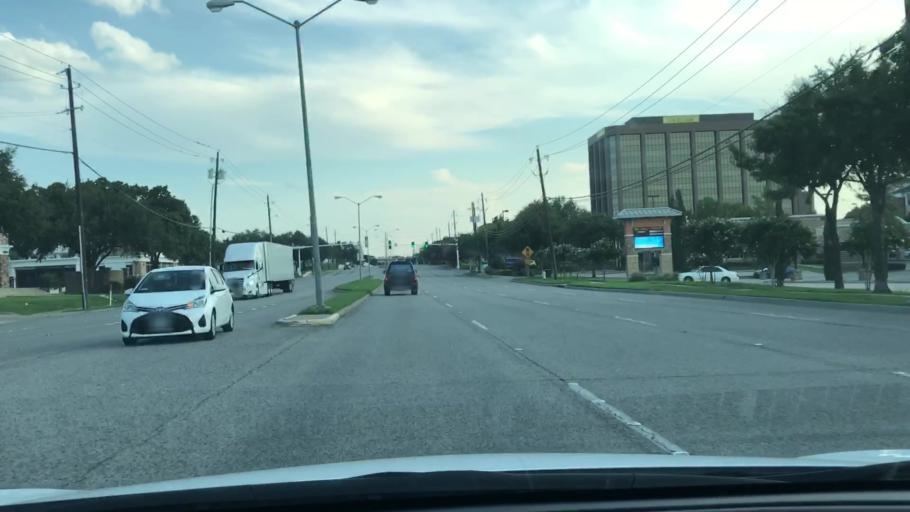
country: US
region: Texas
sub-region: Dallas County
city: Addison
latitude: 32.9347
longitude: -96.8390
